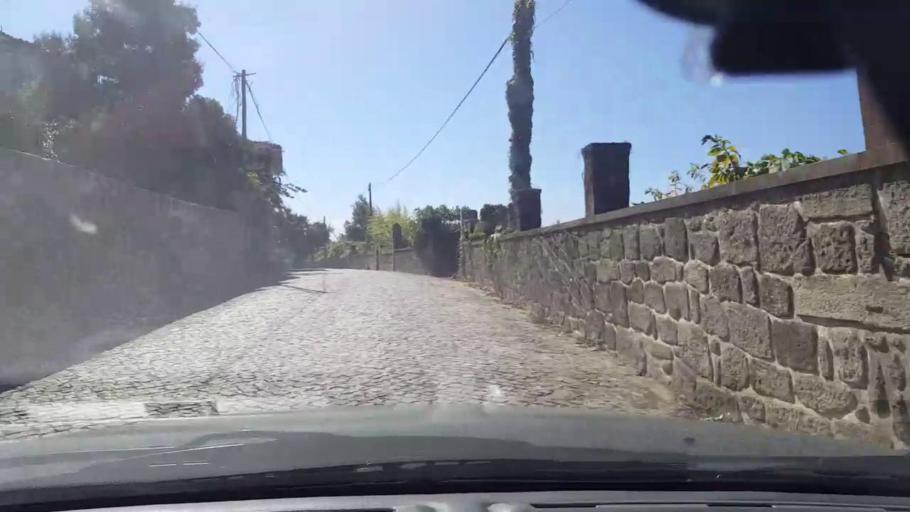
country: PT
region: Porto
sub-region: Maia
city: Gemunde
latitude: 41.2896
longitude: -8.6484
